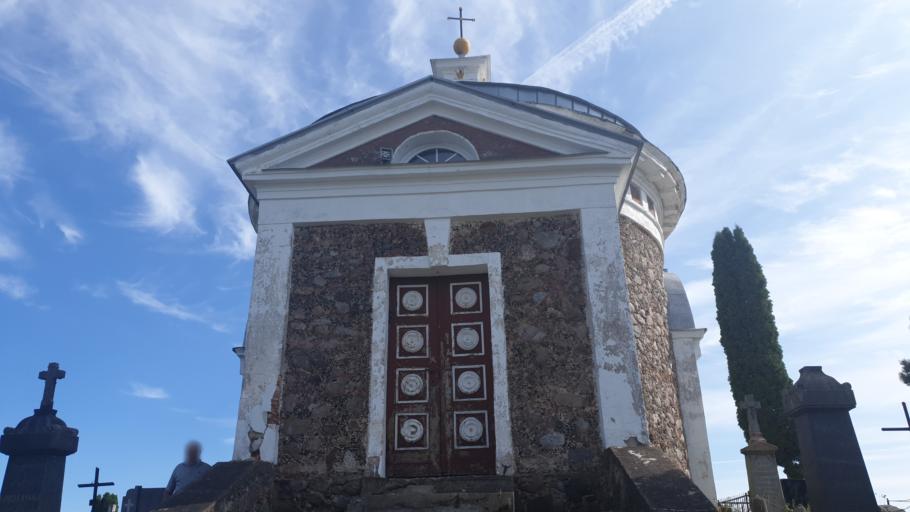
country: LT
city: Salcininkai
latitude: 54.4536
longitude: 25.5108
